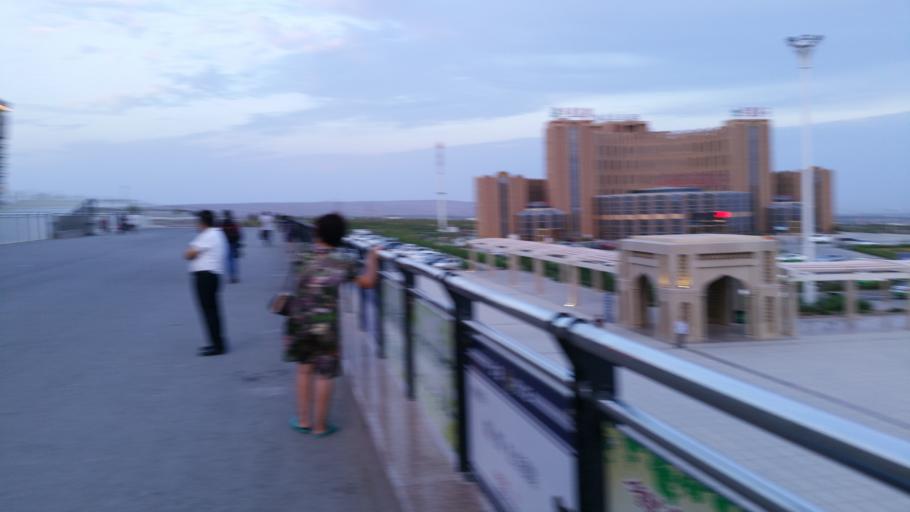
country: CN
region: Xinjiang Uygur Zizhiqu
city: Laochenglu
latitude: 43.0211
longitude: 89.1080
